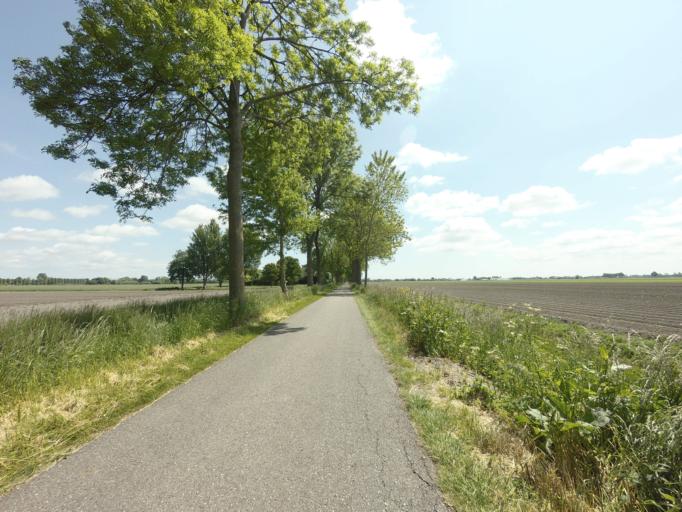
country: NL
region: North Holland
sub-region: Gemeente Beemster
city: Halfweg
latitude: 52.6008
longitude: 4.9188
